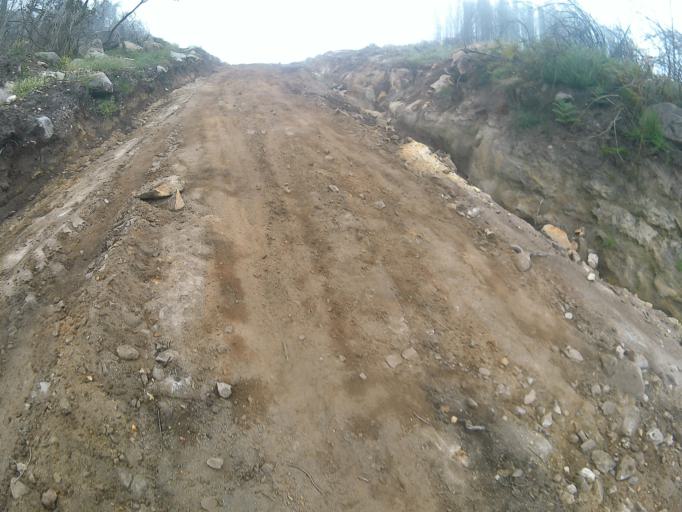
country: PT
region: Viana do Castelo
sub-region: Ponte de Lima
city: Ponte de Lima
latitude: 41.6965
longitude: -8.6082
